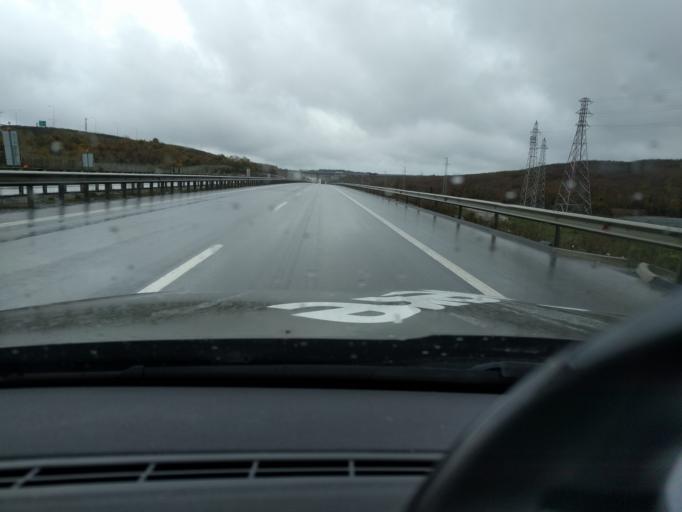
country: TR
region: Istanbul
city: Kemerburgaz
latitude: 41.2234
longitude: 28.8430
